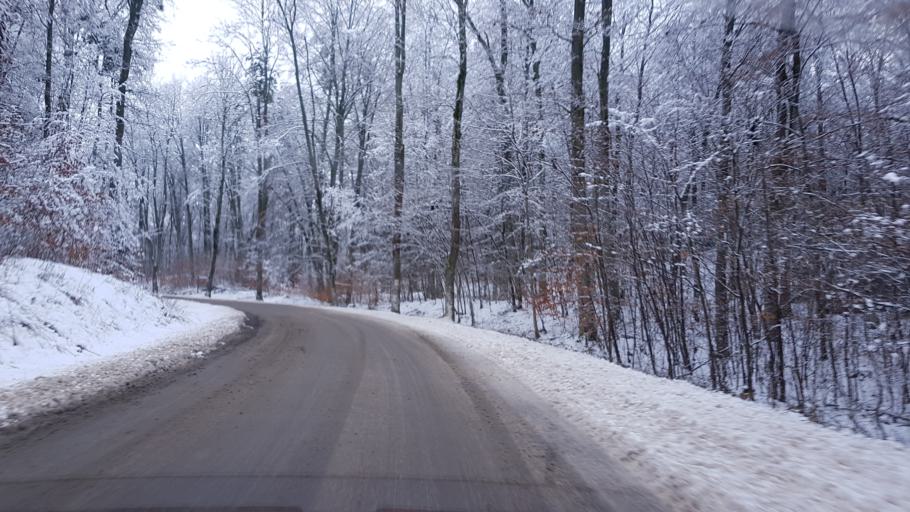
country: PL
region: West Pomeranian Voivodeship
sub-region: Powiat drawski
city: Zlocieniec
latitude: 53.5062
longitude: 16.0052
